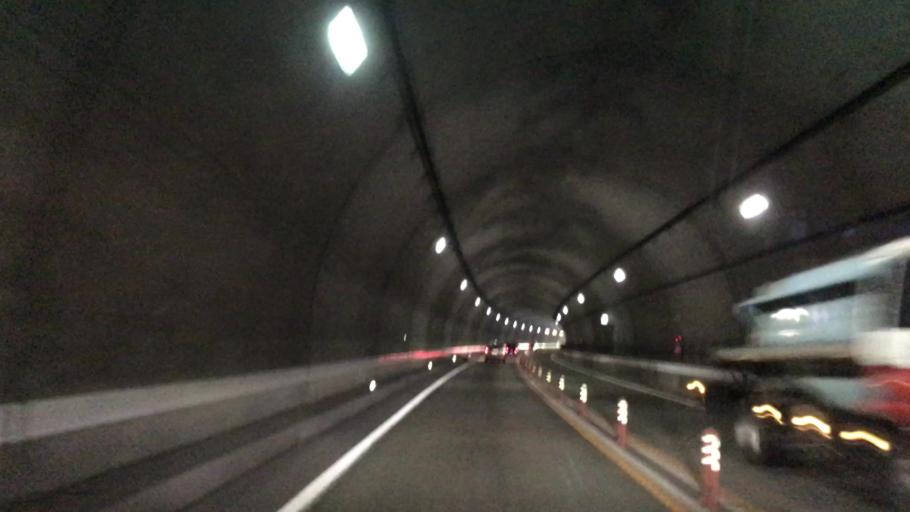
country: JP
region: Hokkaido
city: Shimo-furano
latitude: 42.9729
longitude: 142.3835
